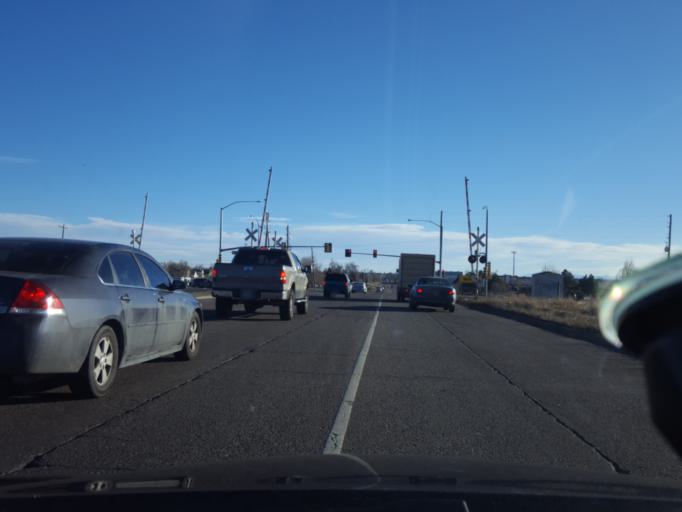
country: US
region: Colorado
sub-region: Adams County
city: Aurora
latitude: 39.7548
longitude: -104.7724
